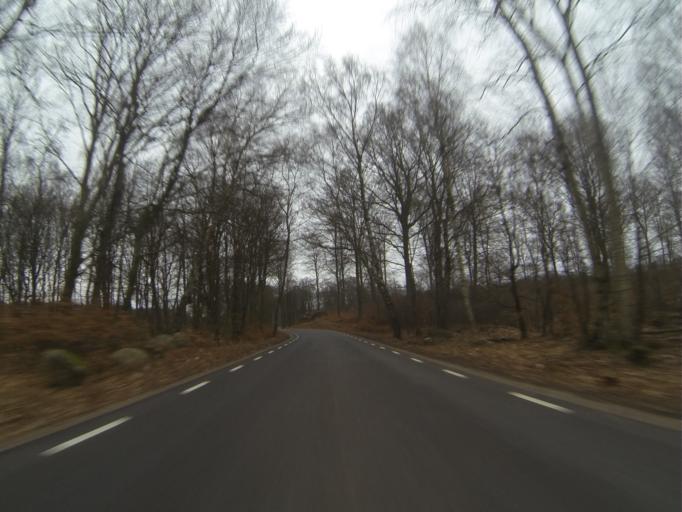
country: SE
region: Skane
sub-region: Lunds Kommun
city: Genarp
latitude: 55.5614
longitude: 13.4333
